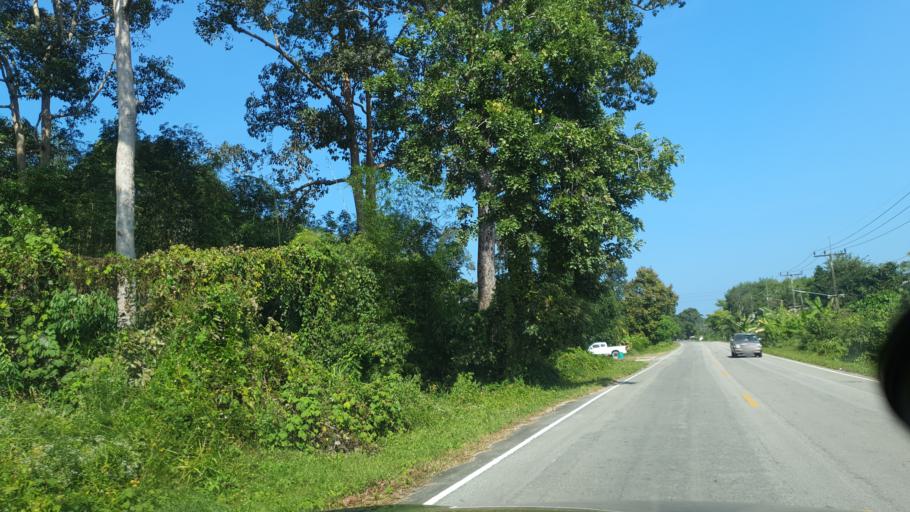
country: TH
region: Surat Thani
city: Tha Chana
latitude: 9.5744
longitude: 99.1815
